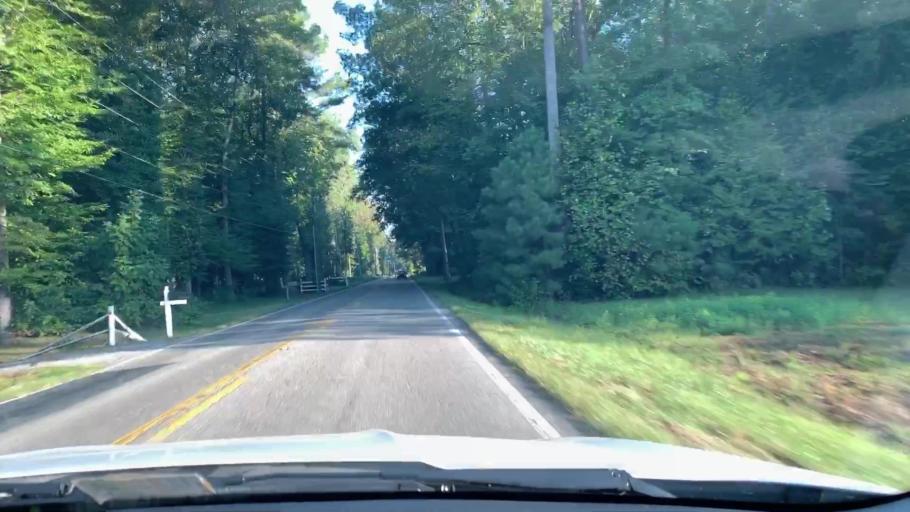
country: US
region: Virginia
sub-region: Gloucester County
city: Gloucester Courthouse
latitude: 37.4679
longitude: -76.4451
